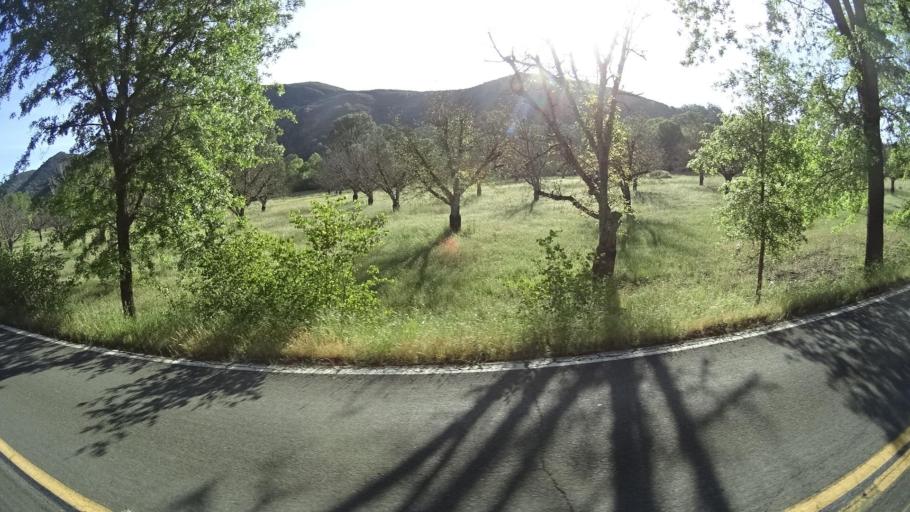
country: US
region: California
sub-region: Lake County
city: Upper Lake
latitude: 39.1274
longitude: -122.9961
